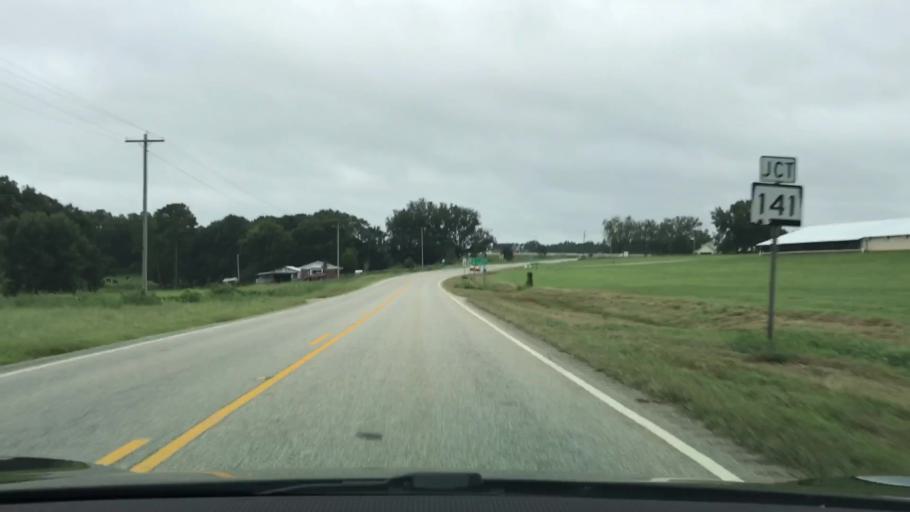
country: US
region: Alabama
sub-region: Coffee County
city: Elba
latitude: 31.3470
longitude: -86.1301
